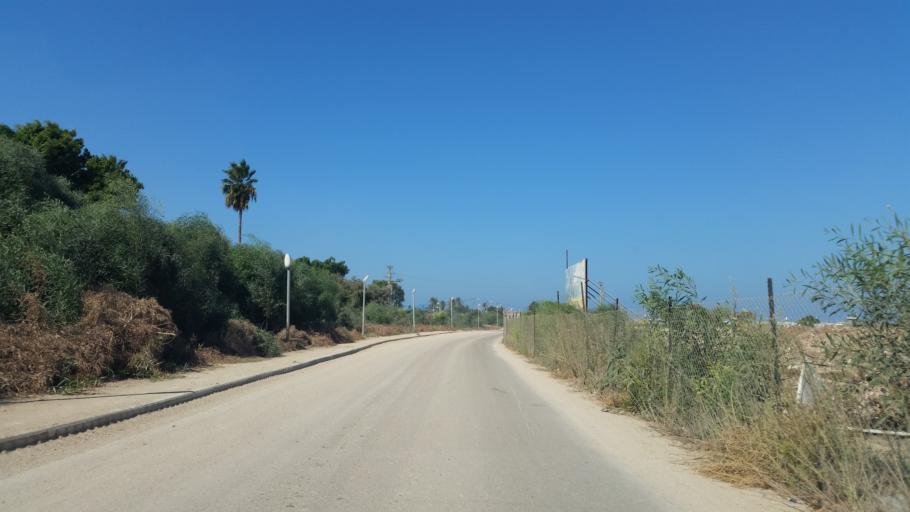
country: IL
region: Haifa
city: `Atlit
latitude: 32.6803
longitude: 34.9326
